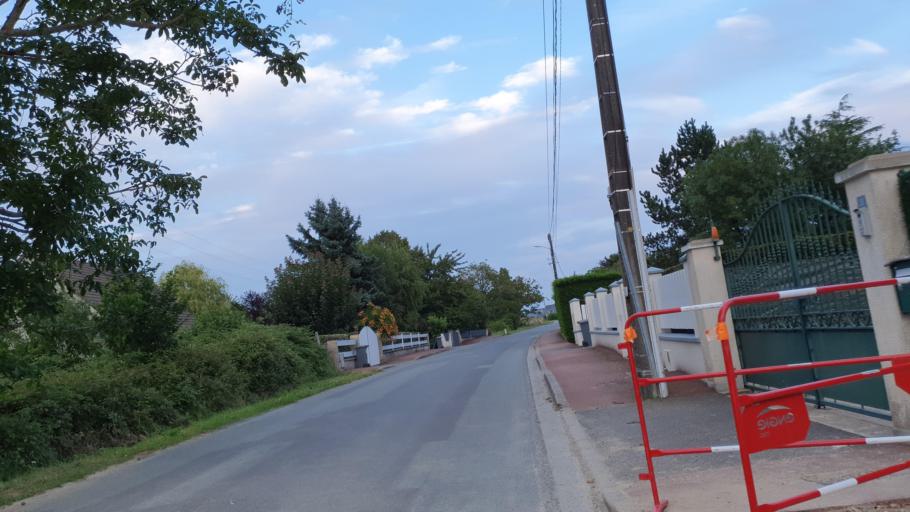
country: FR
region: Centre
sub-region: Departement d'Indre-et-Loire
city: Larcay
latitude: 47.3611
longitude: 0.7659
